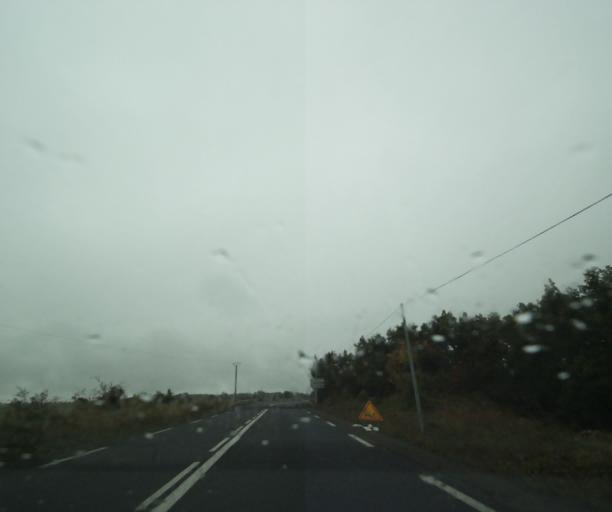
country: FR
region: Midi-Pyrenees
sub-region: Departement de l'Aveyron
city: Millau
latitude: 44.0819
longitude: 3.1245
